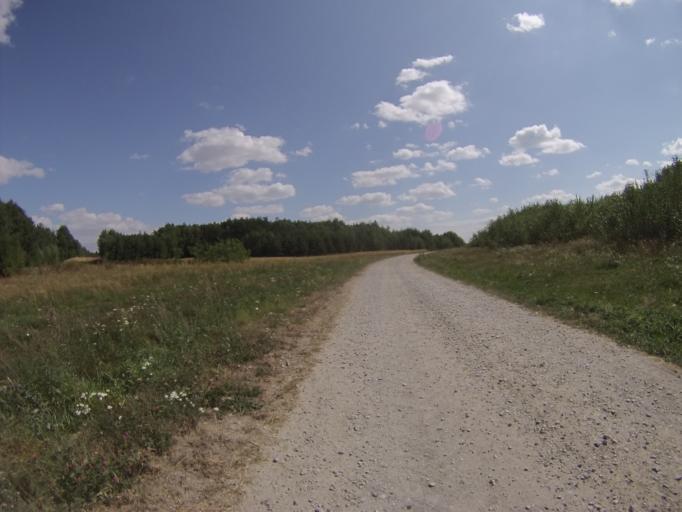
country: PL
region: Swietokrzyskie
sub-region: Powiat kielecki
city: Rakow
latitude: 50.7163
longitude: 21.0509
